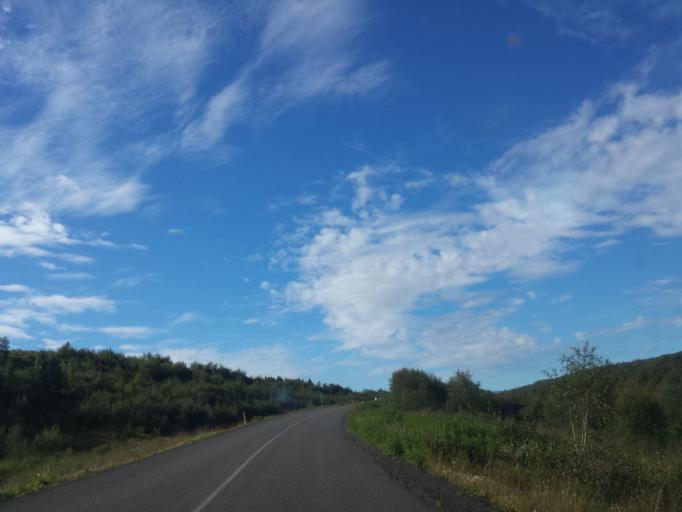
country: IS
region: Northeast
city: Akureyri
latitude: 65.7072
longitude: -17.8965
